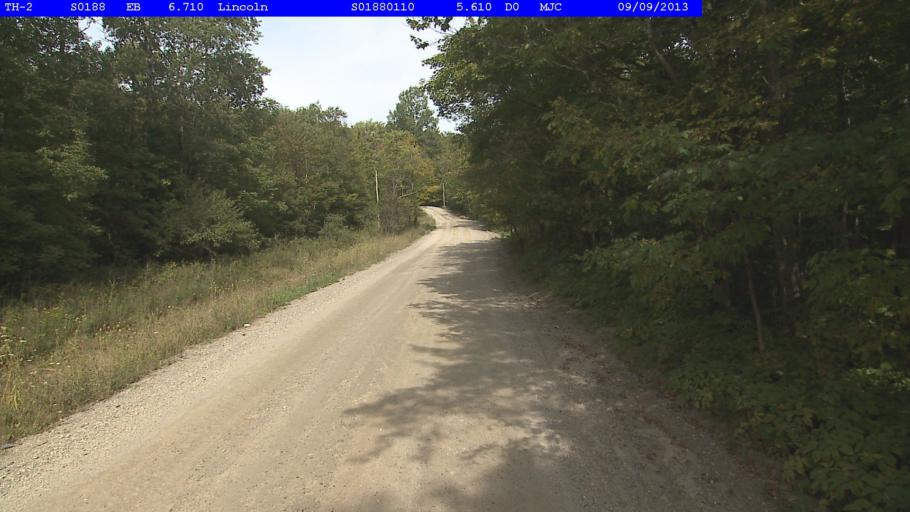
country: US
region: Vermont
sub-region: Addison County
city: Bristol
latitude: 44.0899
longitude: -72.9440
